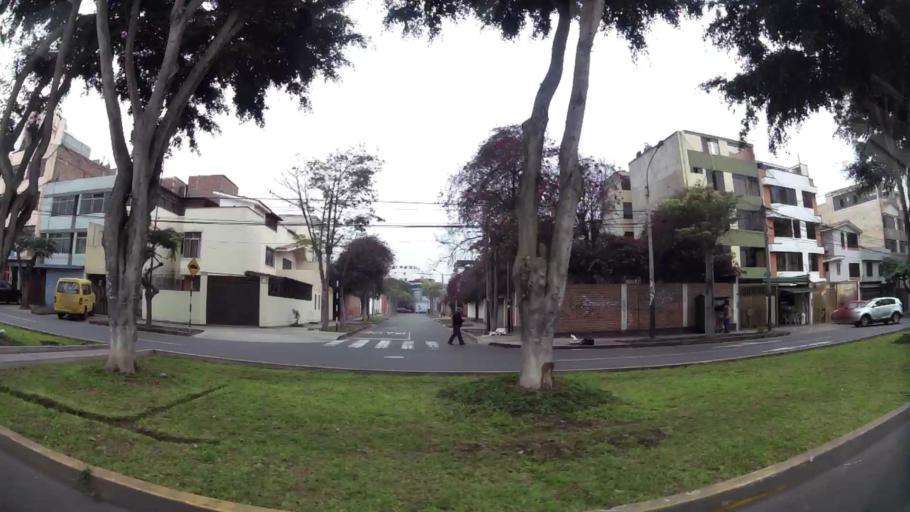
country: PE
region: Lima
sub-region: Lima
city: Surco
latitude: -12.1149
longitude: -77.0071
